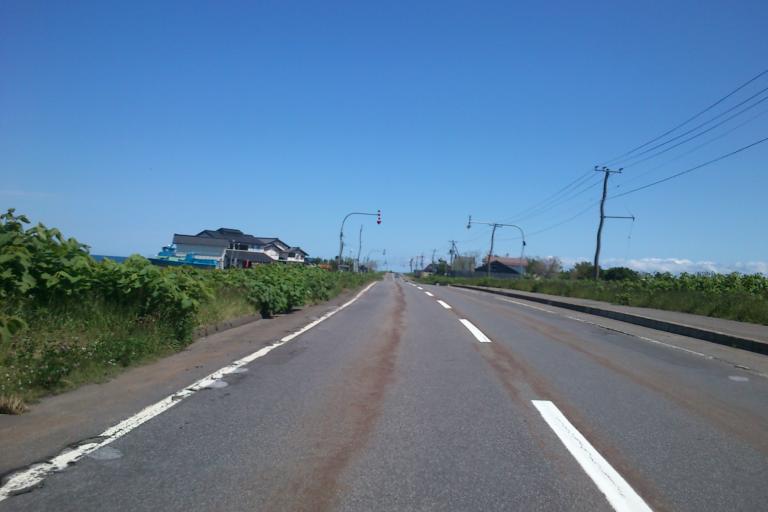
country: JP
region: Hokkaido
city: Rumoi
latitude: 43.8467
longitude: 141.5040
